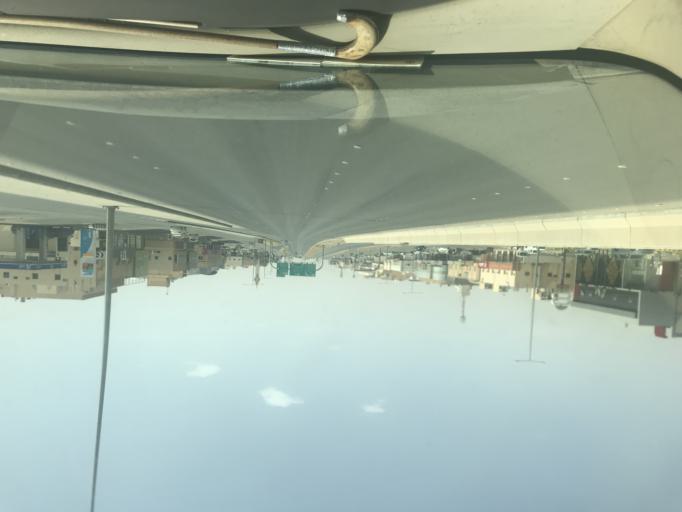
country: SA
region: Ar Riyad
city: Riyadh
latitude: 24.7753
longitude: 46.7091
